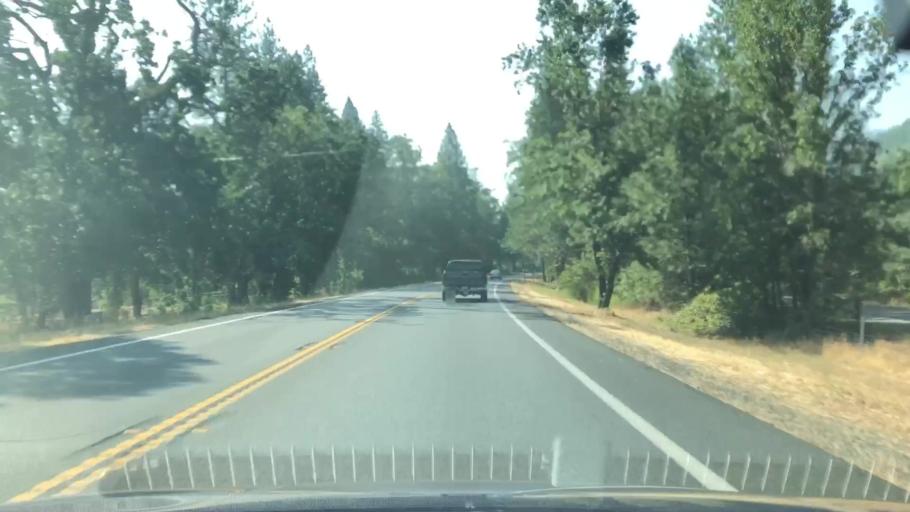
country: US
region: California
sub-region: Lake County
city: Middletown
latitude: 38.7259
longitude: -122.6191
